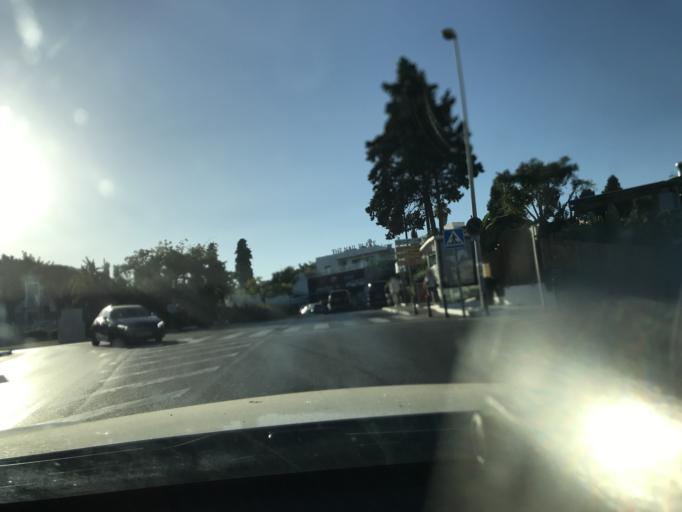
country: ES
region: Andalusia
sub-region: Provincia de Malaga
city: Marbella
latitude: 36.4901
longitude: -4.9570
